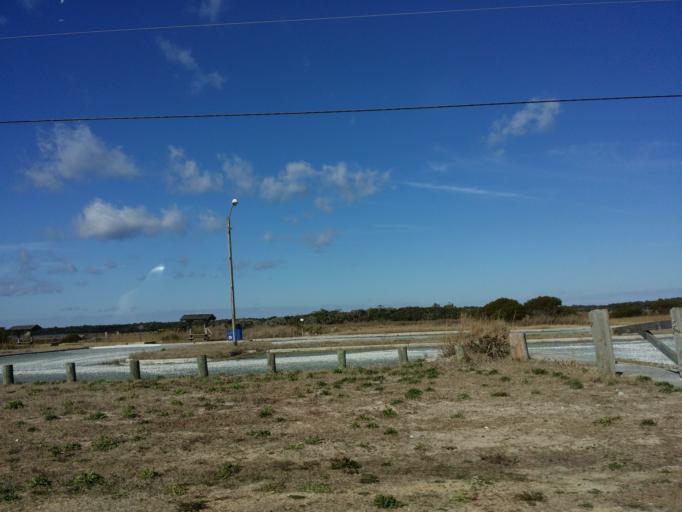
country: US
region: North Carolina
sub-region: Pender County
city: Surf City
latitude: 34.4610
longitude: -77.4854
